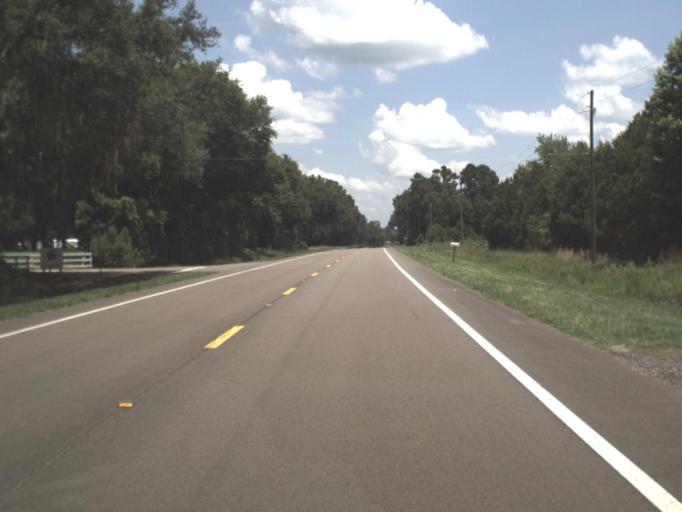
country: US
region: Florida
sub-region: Alachua County
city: Alachua
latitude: 29.7900
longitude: -82.3800
